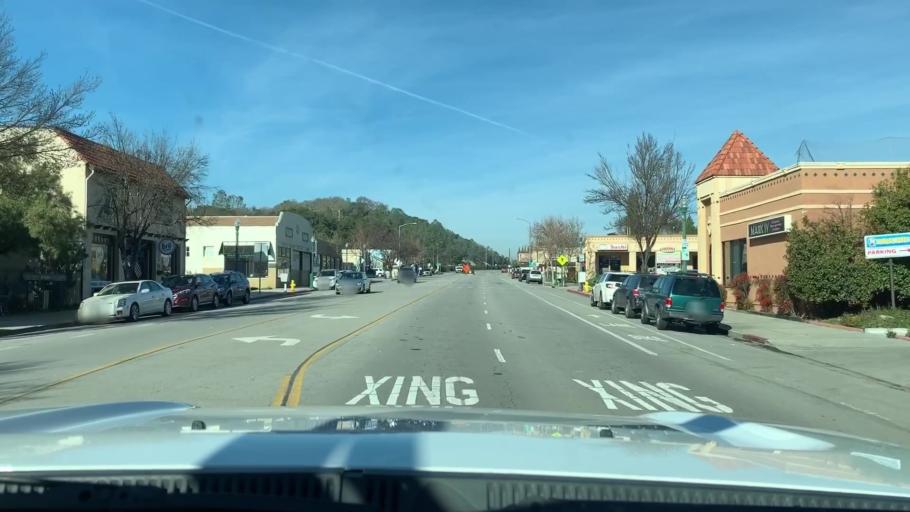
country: US
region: California
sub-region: San Luis Obispo County
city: Atascadero
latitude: 35.4898
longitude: -120.6711
